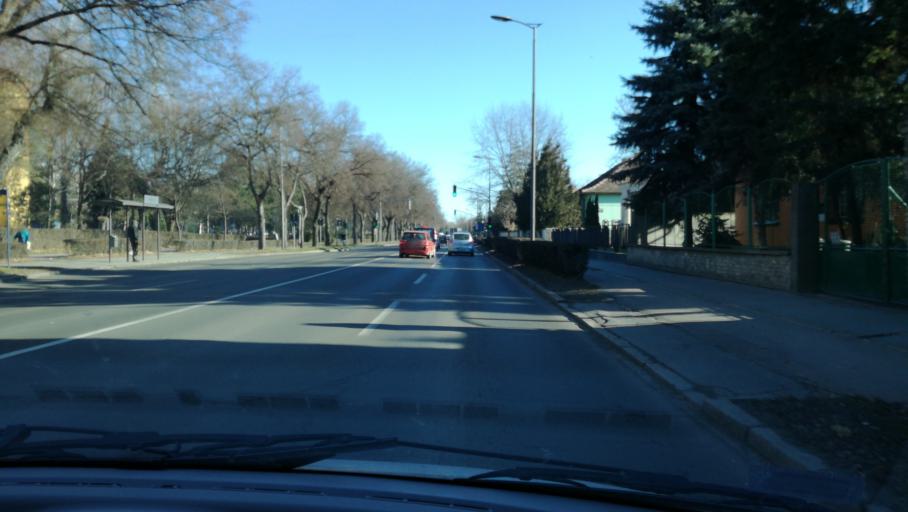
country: RS
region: Autonomna Pokrajina Vojvodina
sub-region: Severnobacki Okrug
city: Subotica
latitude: 46.1000
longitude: 19.6802
